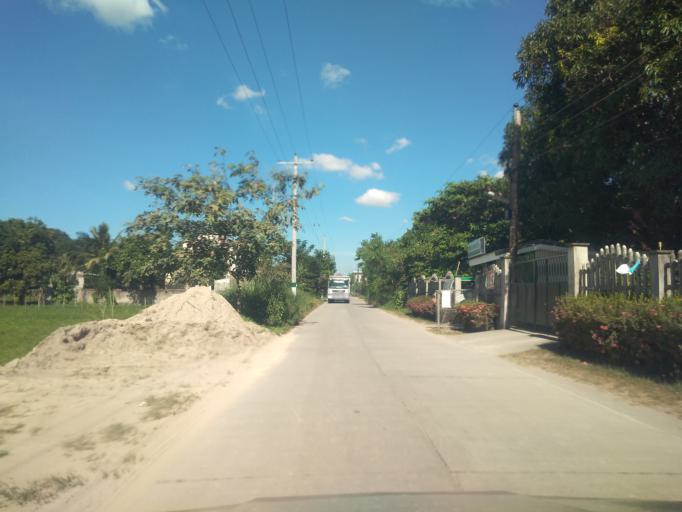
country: PH
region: Central Luzon
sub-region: Province of Pampanga
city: Bacolor
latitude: 15.0071
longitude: 120.6401
